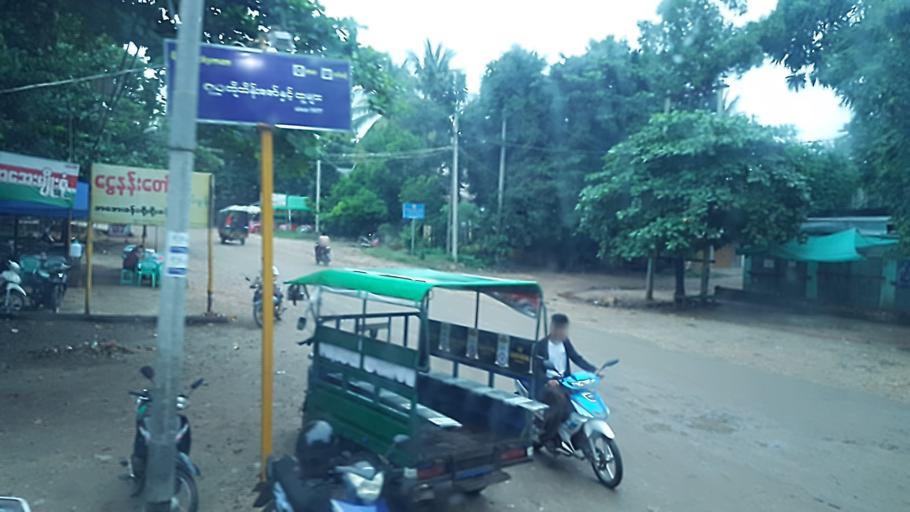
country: MM
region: Magway
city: Magway
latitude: 20.1529
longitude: 94.9411
